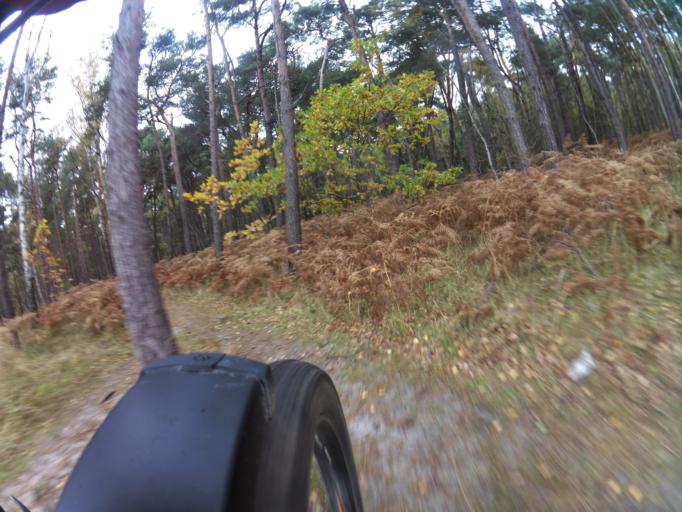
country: PL
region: Pomeranian Voivodeship
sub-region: Powiat pucki
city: Jastarnia
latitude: 54.6882
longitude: 18.7008
